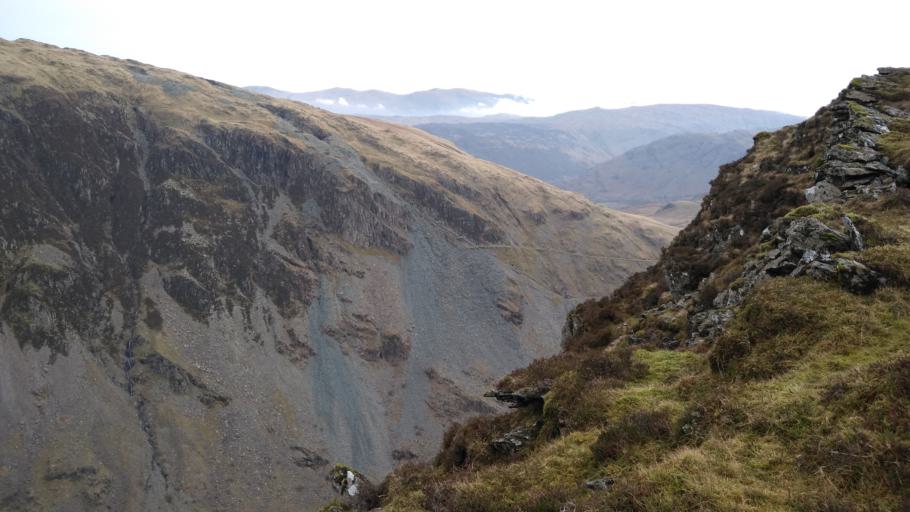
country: GB
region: England
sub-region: Cumbria
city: Keswick
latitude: 54.5153
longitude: -3.2148
